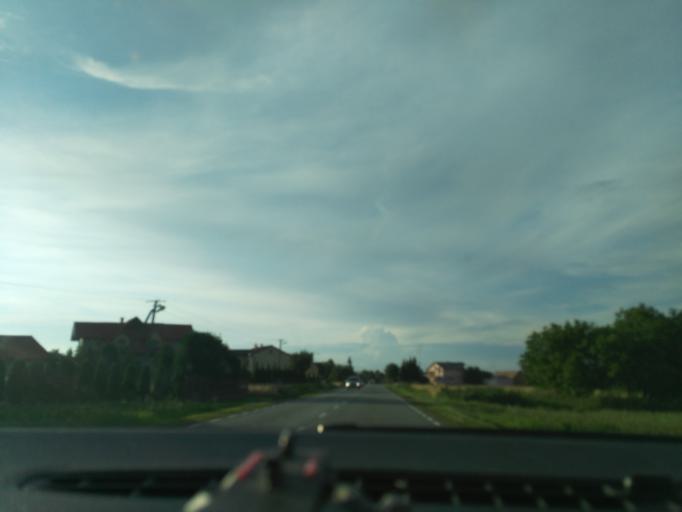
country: PL
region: Lublin Voivodeship
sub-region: Powiat krasnicki
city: Szastarka
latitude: 50.8203
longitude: 22.3159
